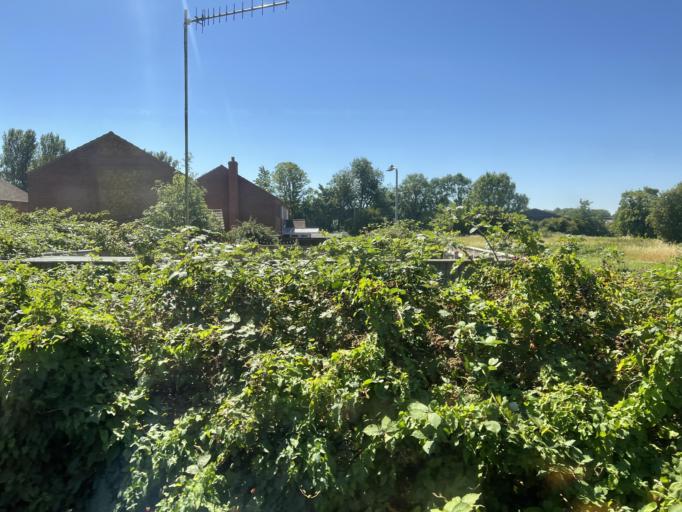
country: GB
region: England
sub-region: Lincolnshire
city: Wainfleet All Saints
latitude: 53.1057
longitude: 0.2332
